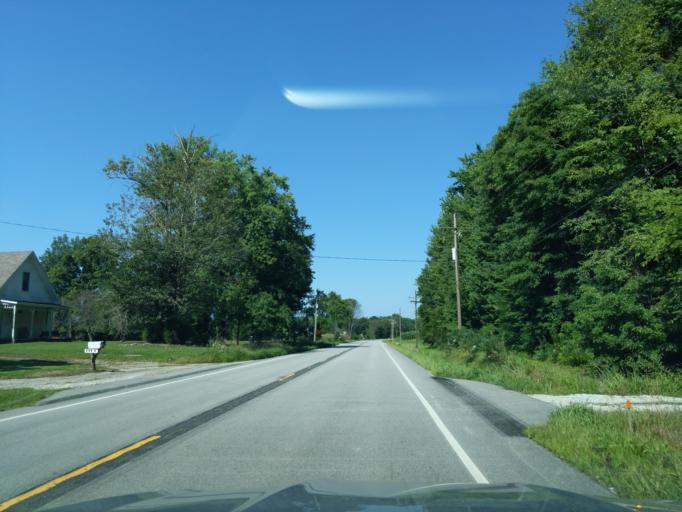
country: US
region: Indiana
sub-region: Ripley County
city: Osgood
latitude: 39.0668
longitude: -85.4136
